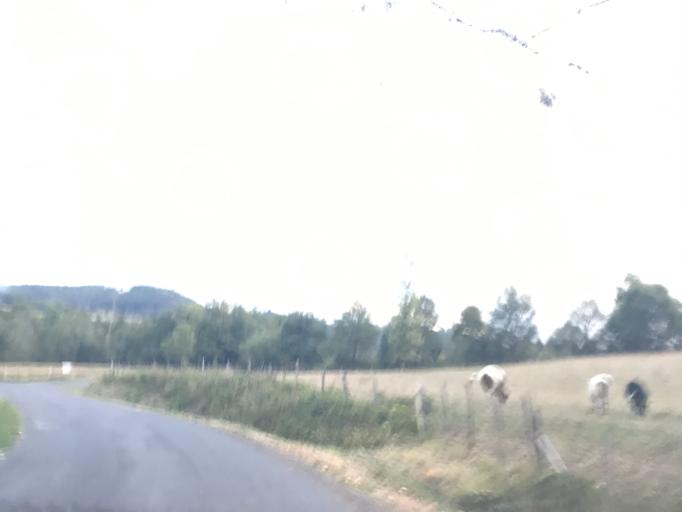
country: FR
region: Auvergne
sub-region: Departement du Puy-de-Dome
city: Escoutoux
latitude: 45.7848
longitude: 3.5864
